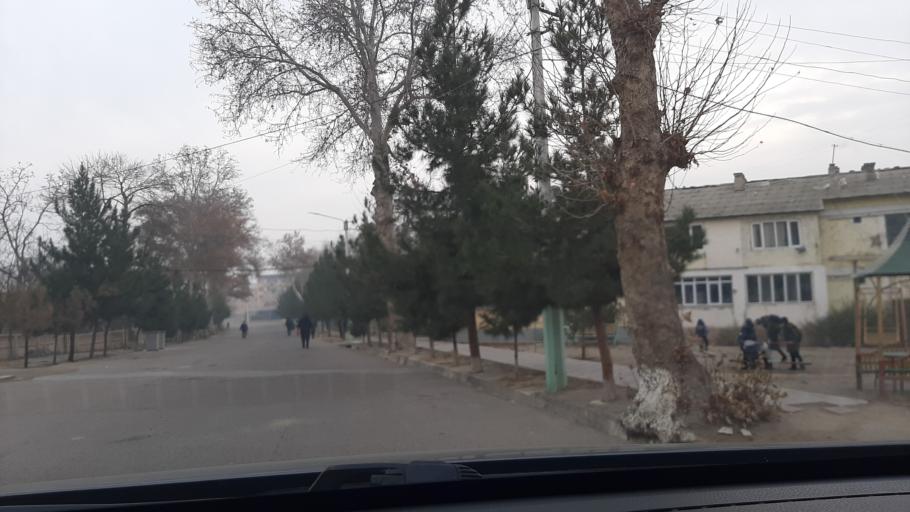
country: TJ
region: Viloyati Sughd
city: Palos
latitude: 40.2628
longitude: 69.7900
